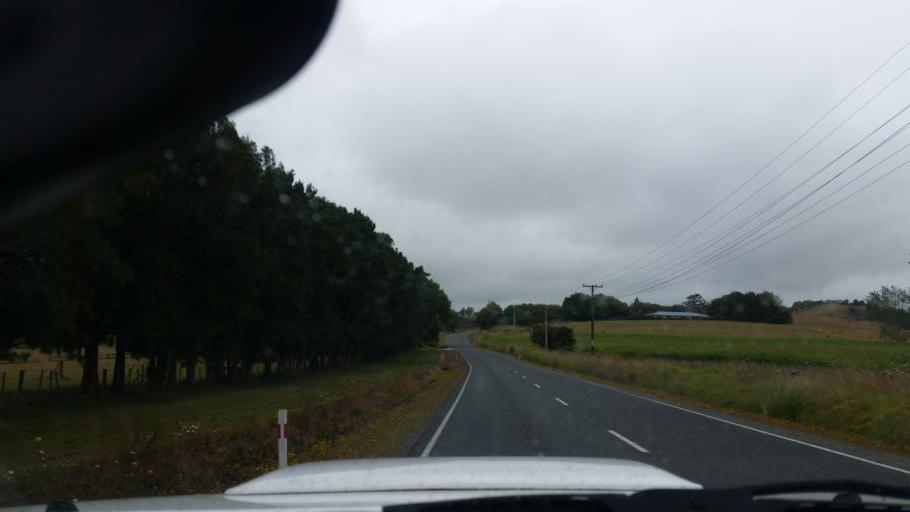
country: NZ
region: Auckland
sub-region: Auckland
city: Wellsford
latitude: -36.1379
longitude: 174.5157
